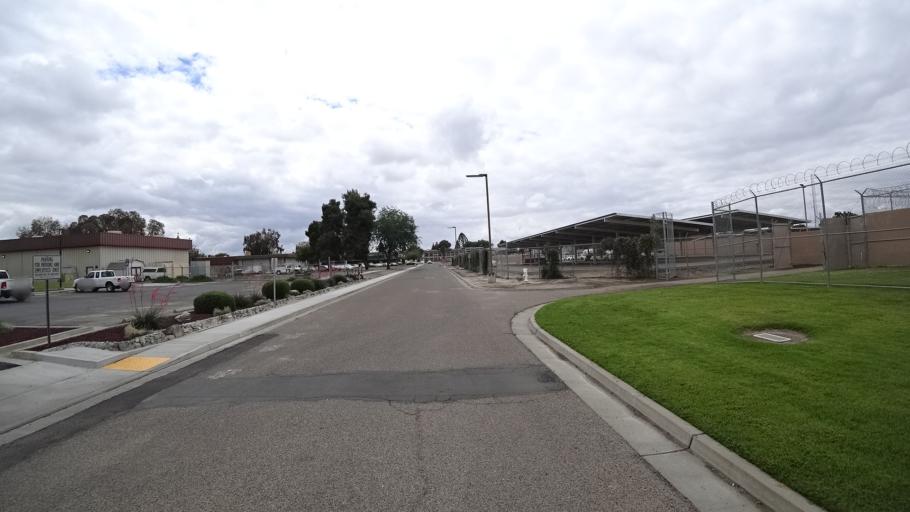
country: US
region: California
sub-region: Kings County
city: Hanford
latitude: 36.3320
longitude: -119.6647
